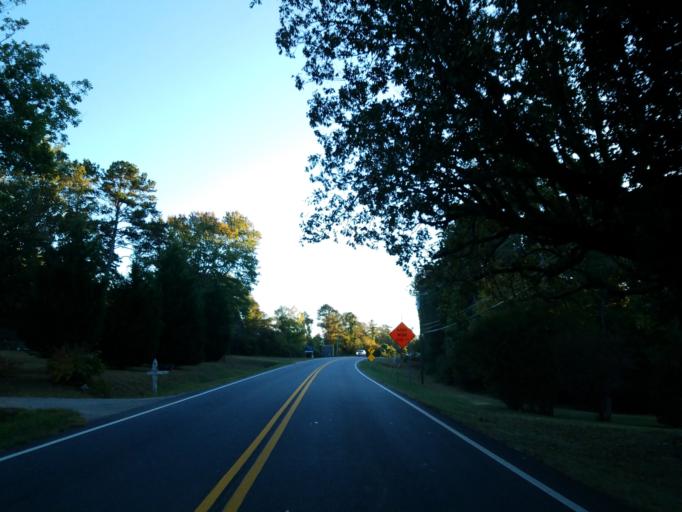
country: US
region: Georgia
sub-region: Forsyth County
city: Cumming
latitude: 34.2536
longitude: -84.1065
